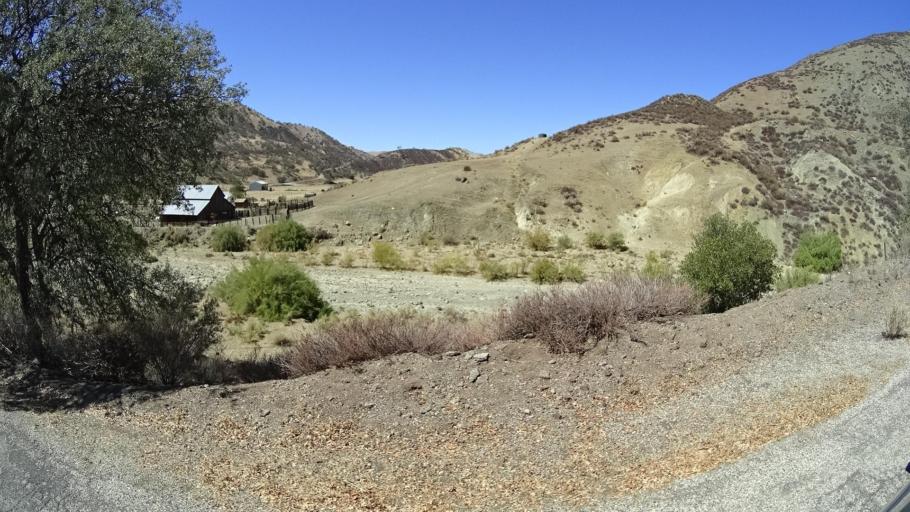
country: US
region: California
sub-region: Monterey County
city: King City
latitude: 36.2922
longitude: -120.8861
